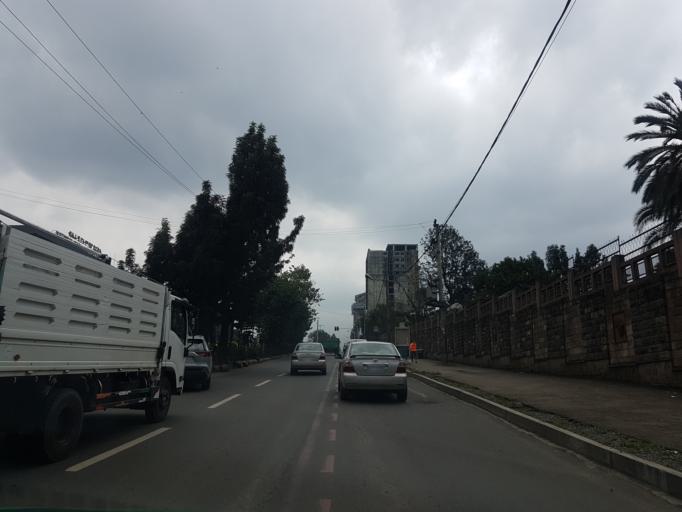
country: ET
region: Adis Abeba
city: Addis Ababa
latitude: 9.0014
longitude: 38.7407
